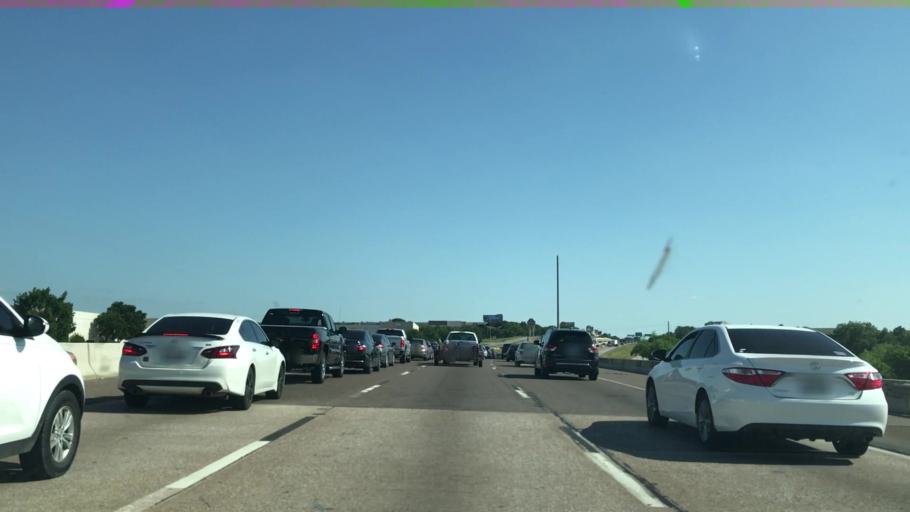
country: US
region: Texas
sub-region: Tarrant County
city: Euless
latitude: 32.8061
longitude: -97.0540
